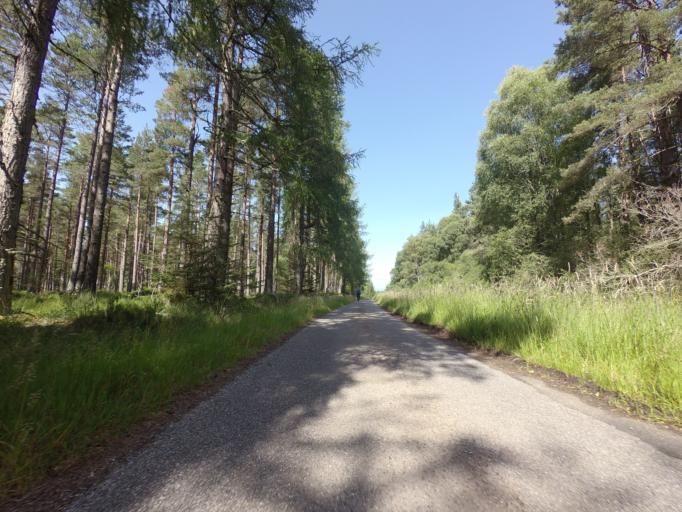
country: GB
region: Scotland
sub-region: Highland
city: Nairn
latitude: 57.4986
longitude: -3.9689
